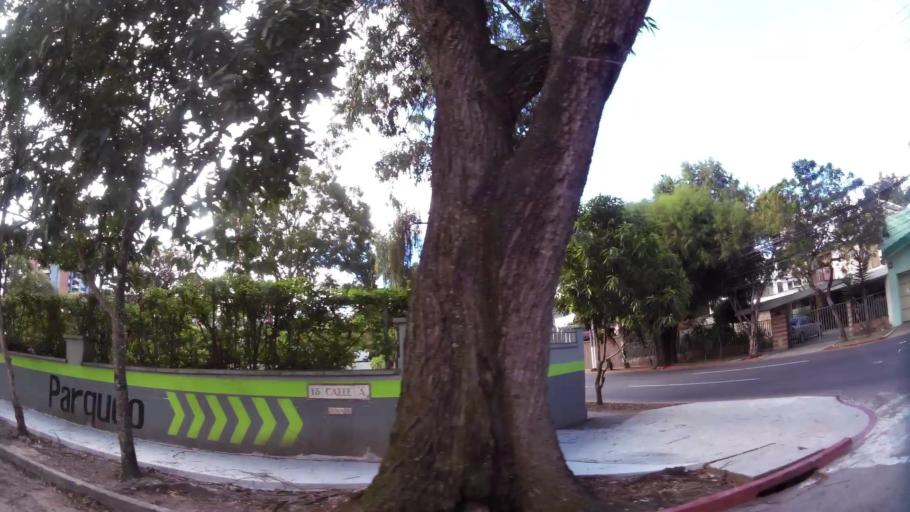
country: GT
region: Guatemala
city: Santa Catarina Pinula
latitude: 14.5980
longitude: -90.5111
